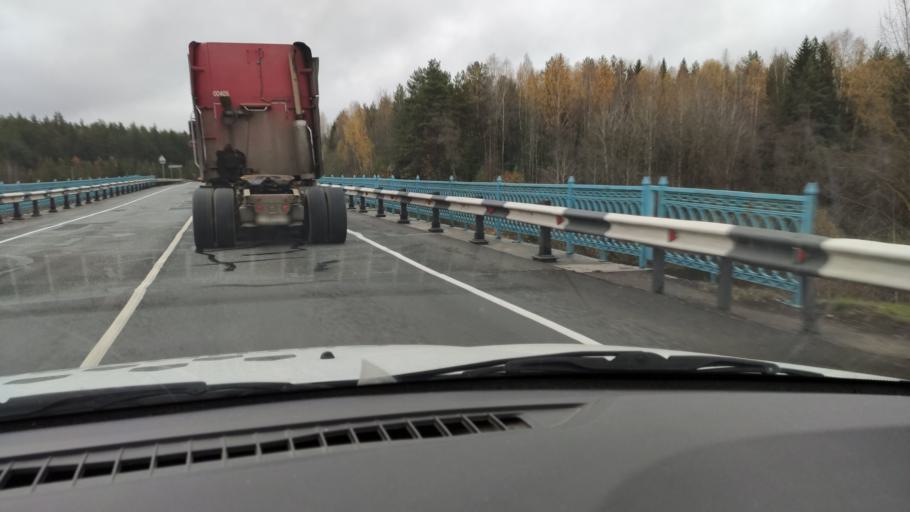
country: RU
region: Kirov
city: Belaya Kholunitsa
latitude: 58.8358
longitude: 50.6888
